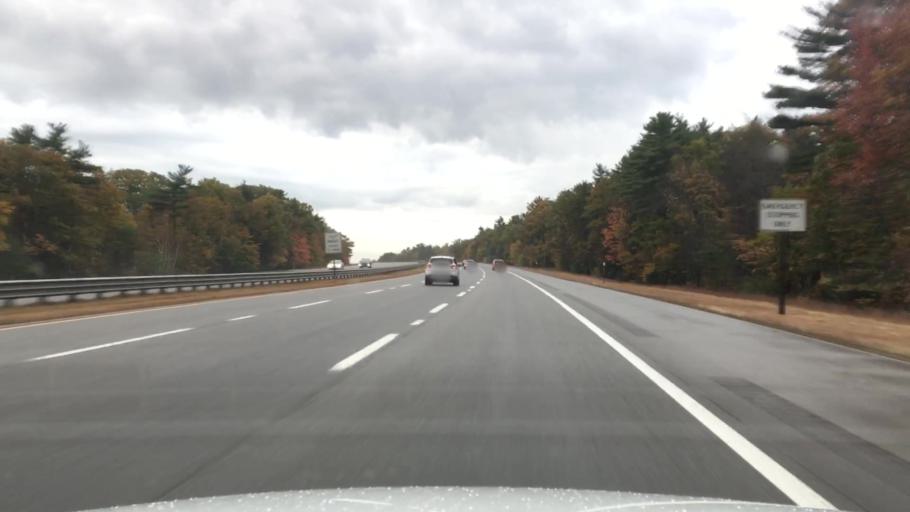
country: US
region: Maine
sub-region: York County
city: Ogunquit
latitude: 43.2333
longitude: -70.6347
